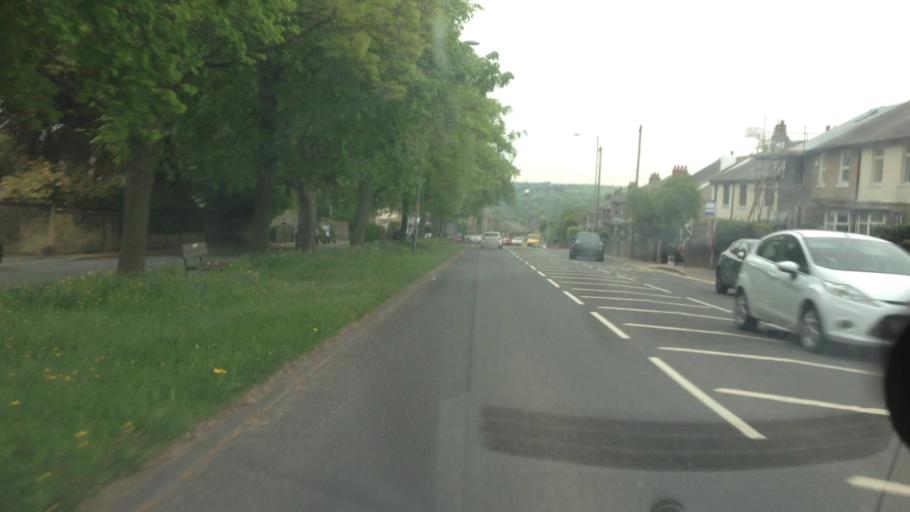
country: GB
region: England
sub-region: Calderdale
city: Brighouse
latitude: 53.6878
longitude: -1.7949
